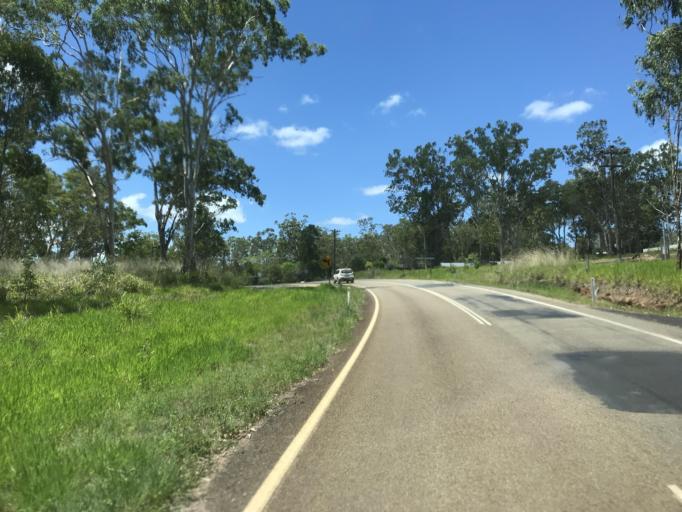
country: AU
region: Queensland
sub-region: Tablelands
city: Atherton
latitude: -17.4124
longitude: 145.3930
